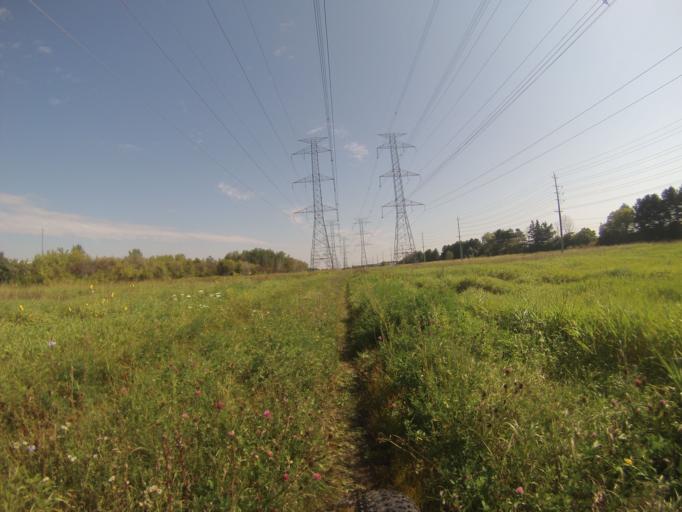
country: CA
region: Ontario
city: Ottawa
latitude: 45.3759
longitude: -75.6350
